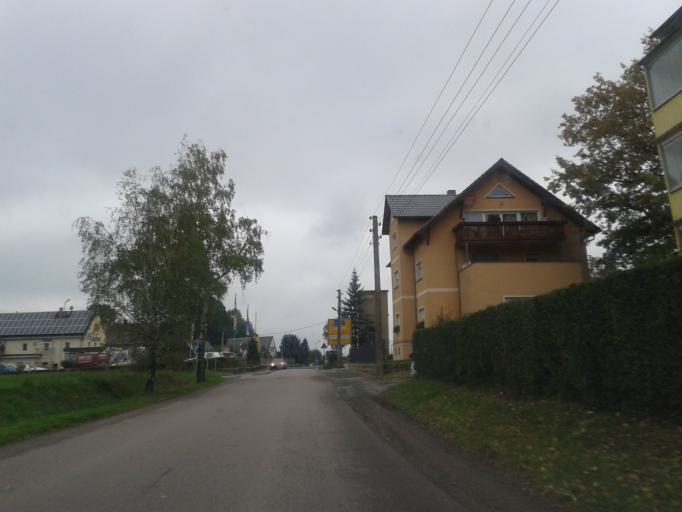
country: DE
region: Saxony
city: Nossen
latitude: 51.0529
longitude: 13.3461
